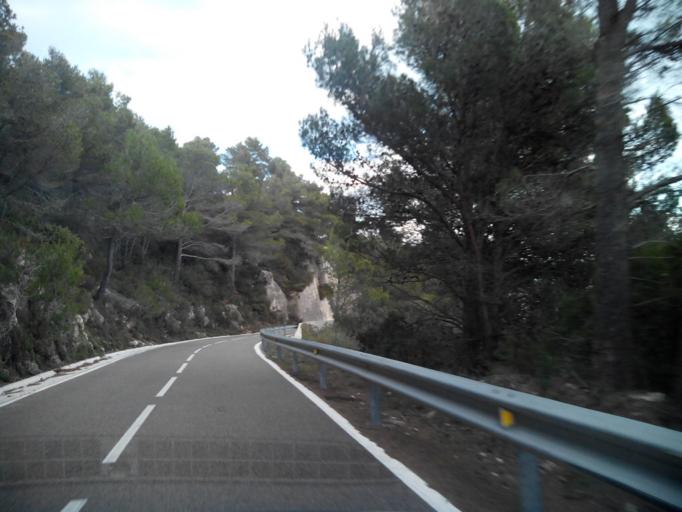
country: ES
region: Catalonia
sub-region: Provincia de Tarragona
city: Vilaplana
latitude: 41.2340
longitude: 1.0602
